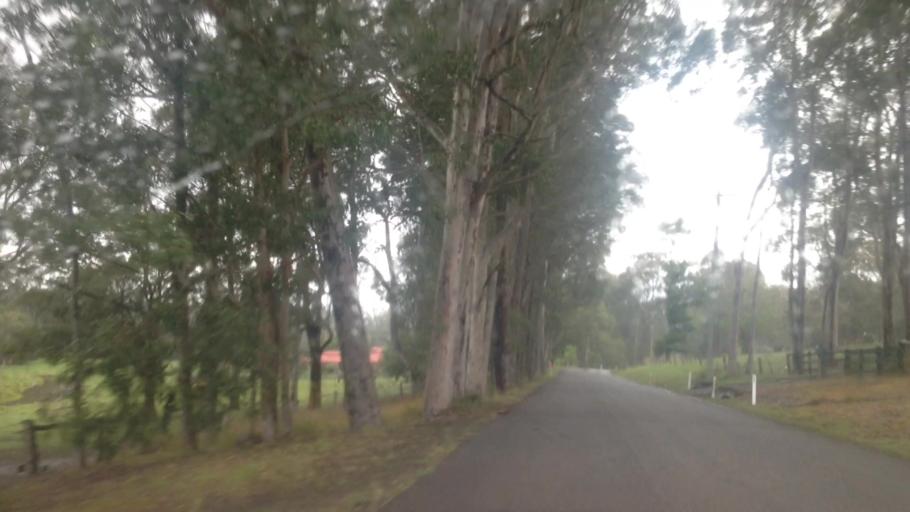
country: AU
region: New South Wales
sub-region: Wyong Shire
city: Little Jilliby
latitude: -33.2084
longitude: 151.3688
